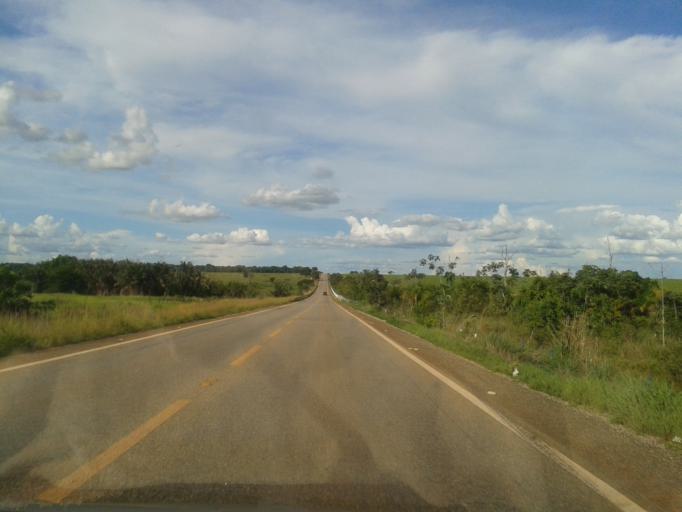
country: BR
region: Goias
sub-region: Mozarlandia
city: Mozarlandia
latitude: -14.3476
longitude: -50.4211
